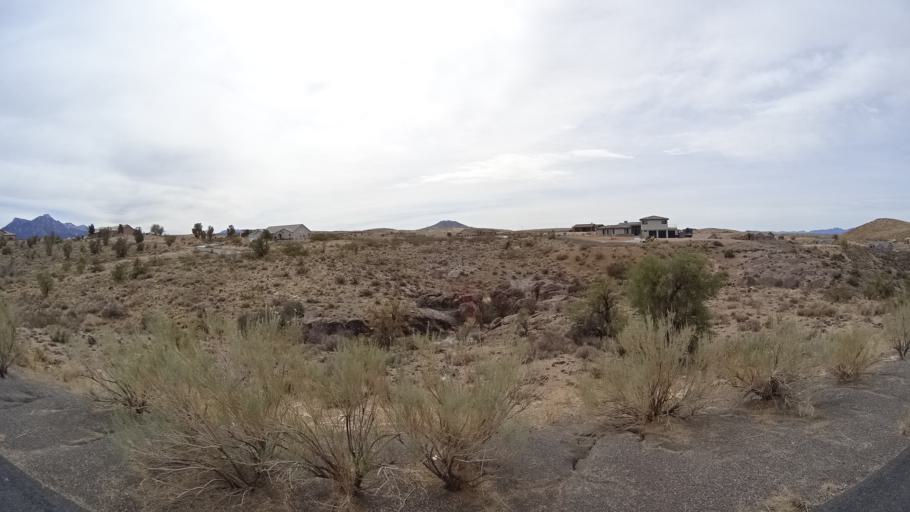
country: US
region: Arizona
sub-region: Mohave County
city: Kingman
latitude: 35.1803
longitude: -114.0002
